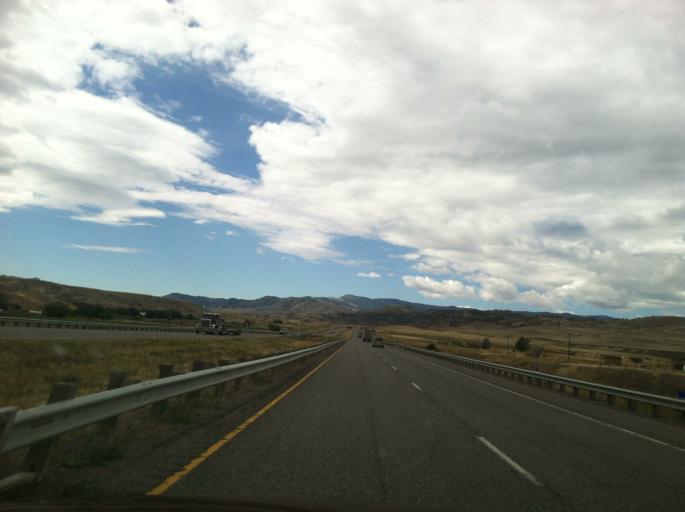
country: US
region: Montana
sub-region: Park County
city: Livingston
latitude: 45.6513
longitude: -110.6119
